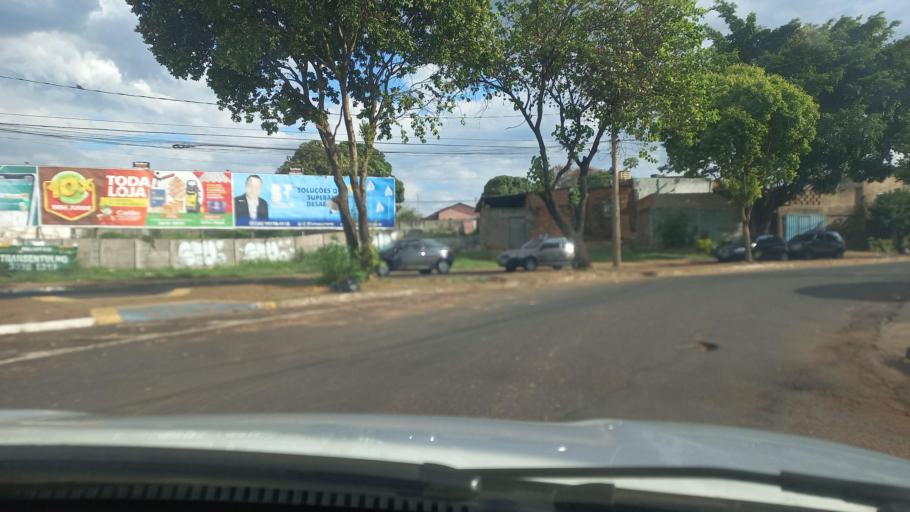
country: BR
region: Minas Gerais
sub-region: Uberaba
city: Uberaba
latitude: -19.7584
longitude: -47.9090
